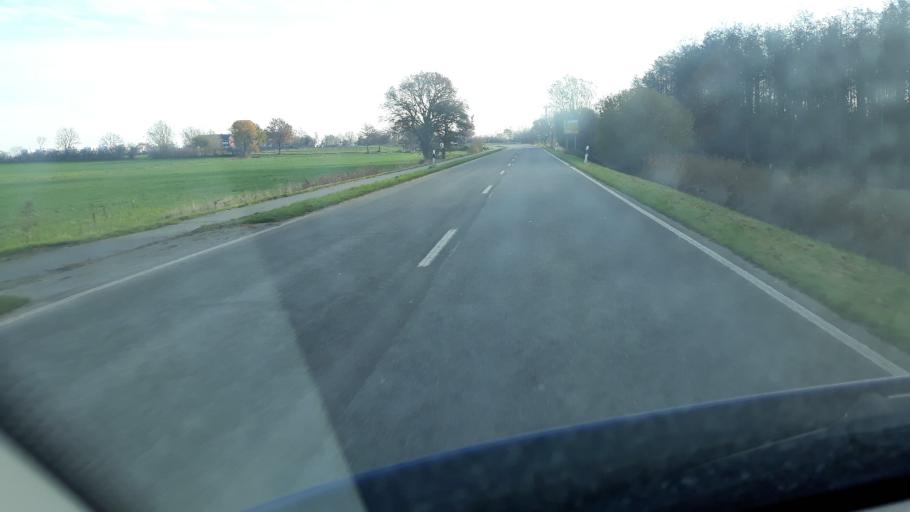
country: DE
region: Schleswig-Holstein
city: Maasholm
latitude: 54.6602
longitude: 10.0020
